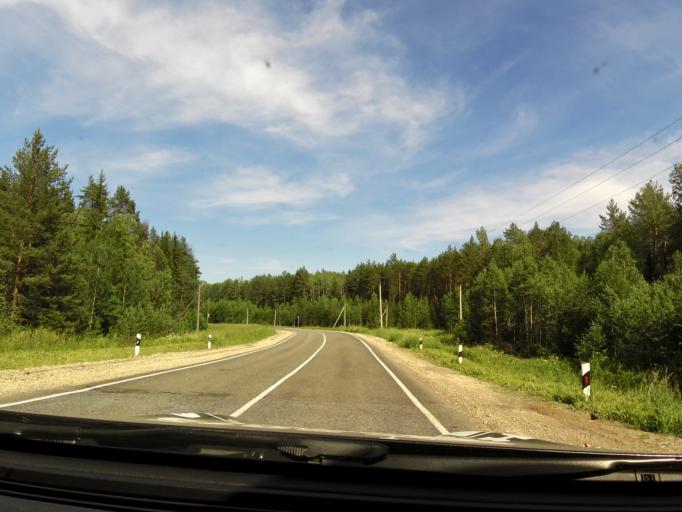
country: RU
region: Kirov
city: Belaya Kholunitsa
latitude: 58.8288
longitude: 50.6766
